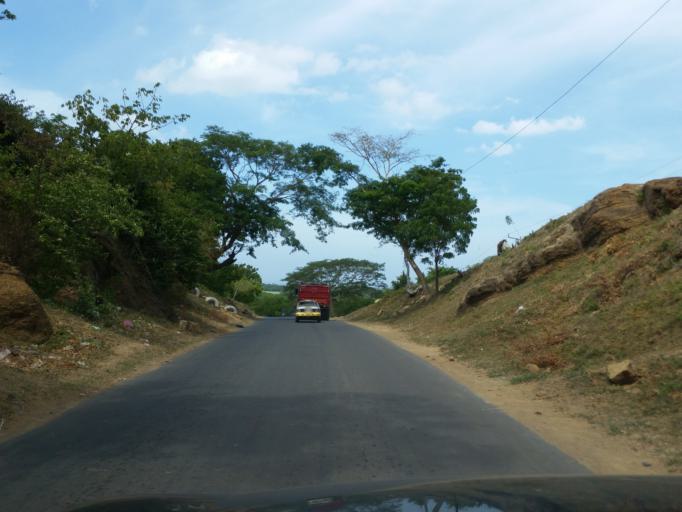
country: NI
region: Managua
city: Masachapa
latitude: 11.8117
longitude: -86.4892
